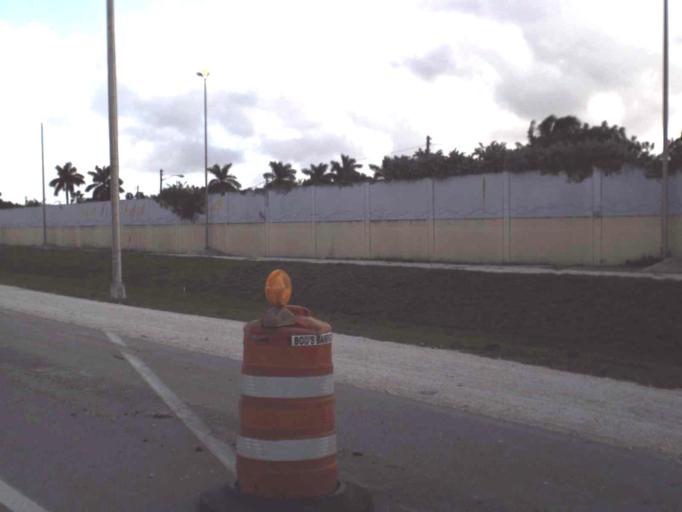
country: US
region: Florida
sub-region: Miami-Dade County
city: Norland
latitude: 25.9365
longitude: -80.2175
